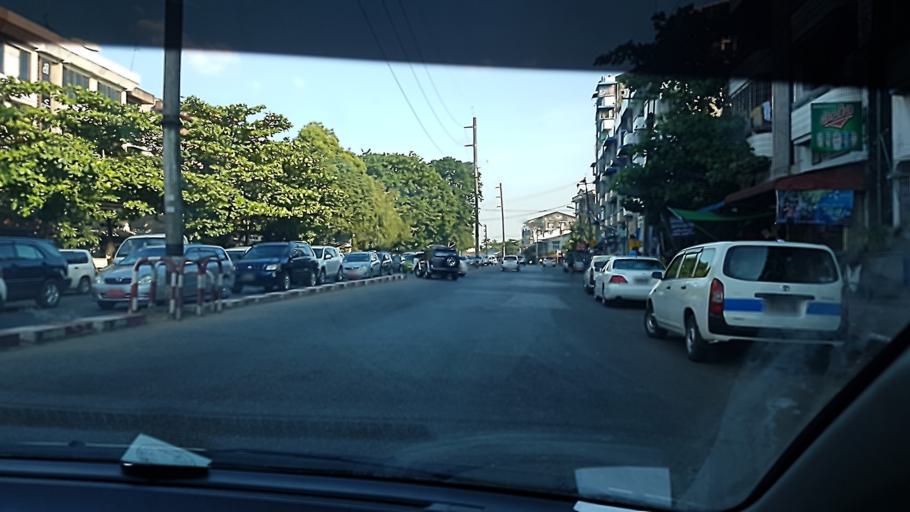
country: MM
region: Yangon
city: Yangon
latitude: 16.8204
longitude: 96.1766
